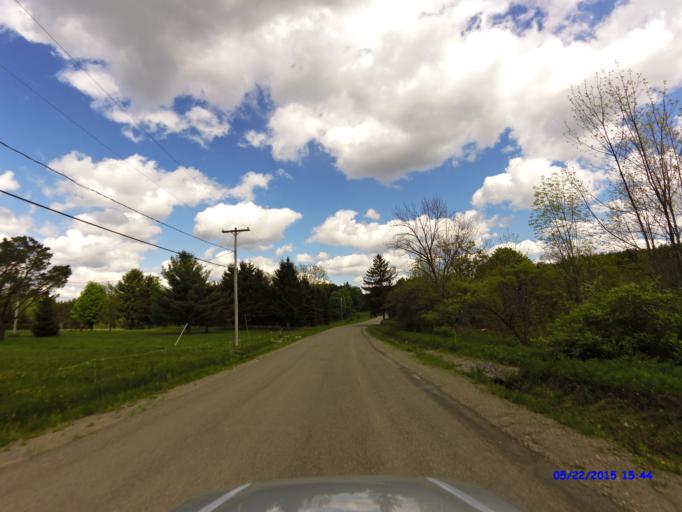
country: US
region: New York
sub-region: Cattaraugus County
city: Franklinville
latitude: 42.3148
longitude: -78.5527
